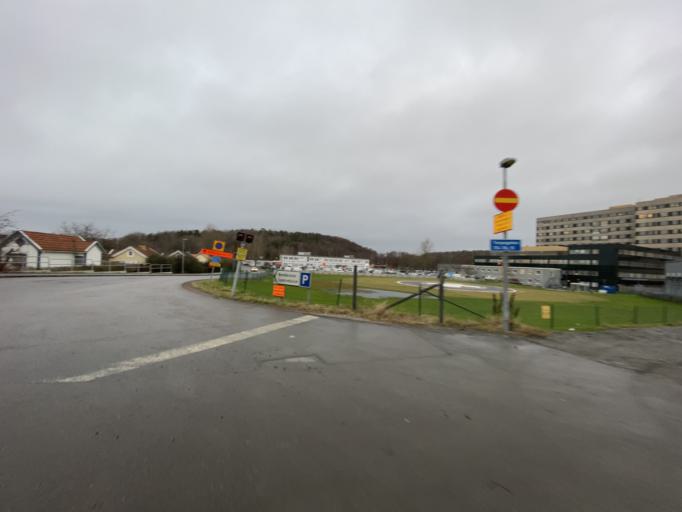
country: SE
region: Vaestra Goetaland
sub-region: Goteborg
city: Eriksbo
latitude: 57.7206
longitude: 12.0471
